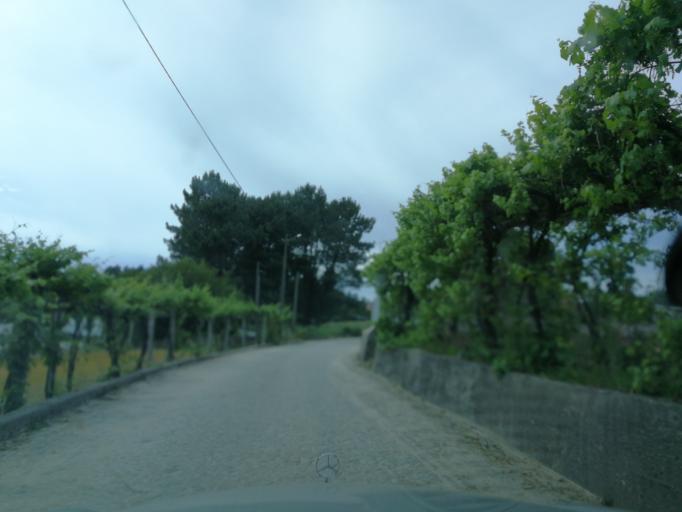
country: PT
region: Braga
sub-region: Braga
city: Oliveira
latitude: 41.4773
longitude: -8.4804
